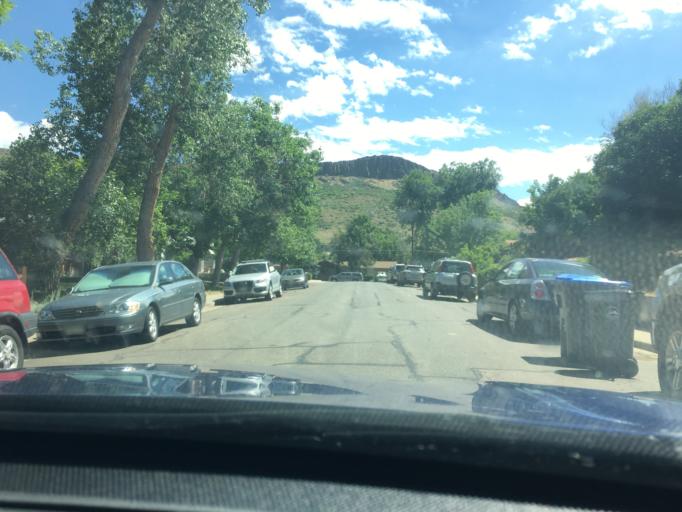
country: US
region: Colorado
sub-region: Jefferson County
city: Golden
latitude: 39.7648
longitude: -105.2281
